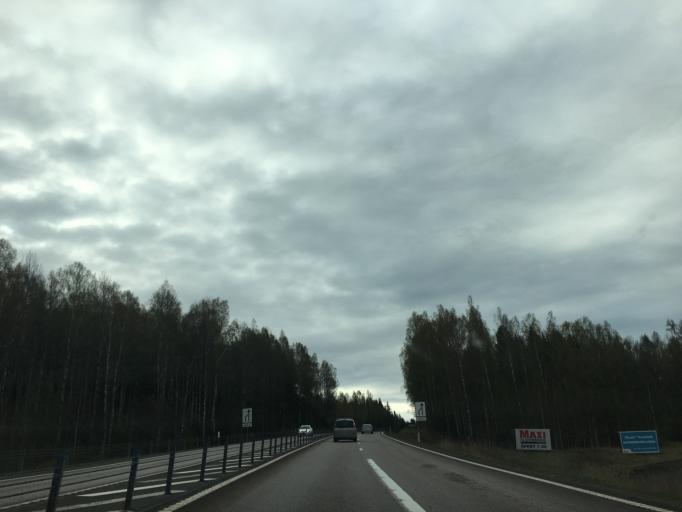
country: SE
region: Vaermland
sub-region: Kristinehamns Kommun
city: Kristinehamn
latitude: 59.3544
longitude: 14.0698
